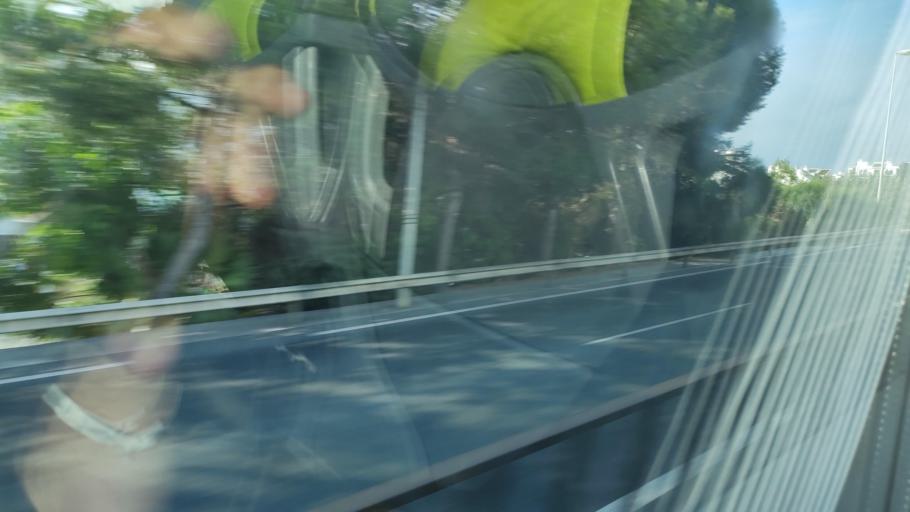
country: ES
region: Andalusia
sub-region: Provincia de Malaga
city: Fuengirola
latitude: 36.4952
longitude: -4.6906
